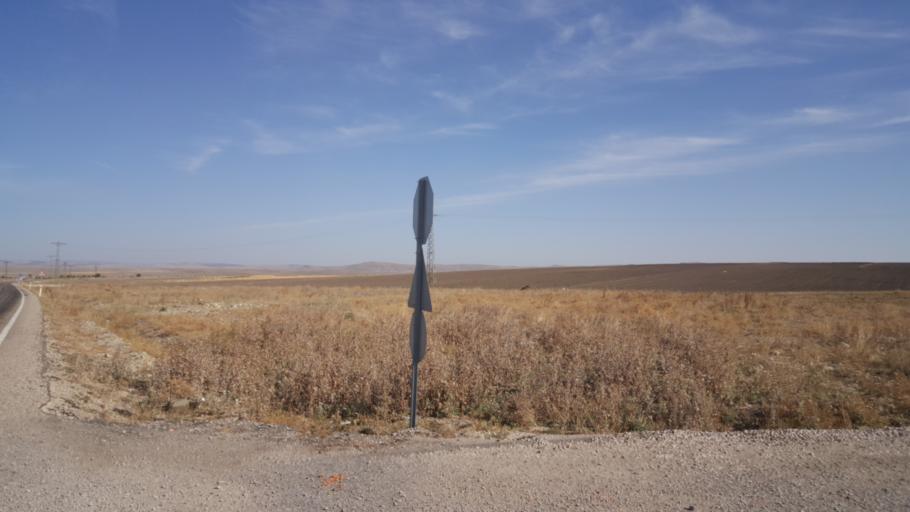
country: TR
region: Ankara
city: Yenice
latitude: 39.3723
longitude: 32.7265
